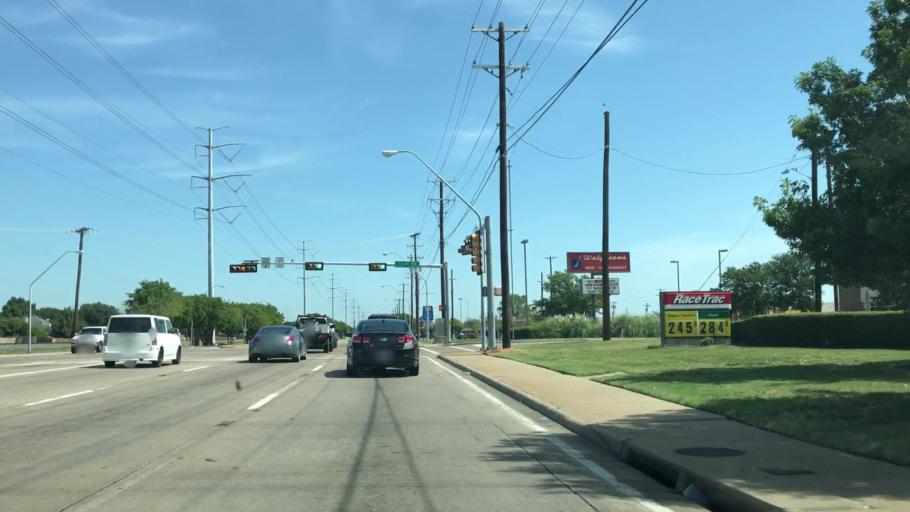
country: US
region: Texas
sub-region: Dallas County
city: Garland
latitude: 32.9391
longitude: -96.6230
